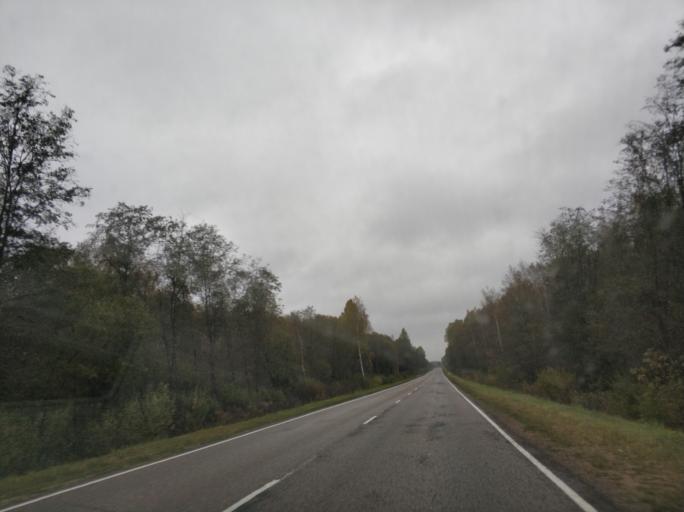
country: BY
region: Vitebsk
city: Rasony
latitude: 56.0828
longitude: 28.7175
